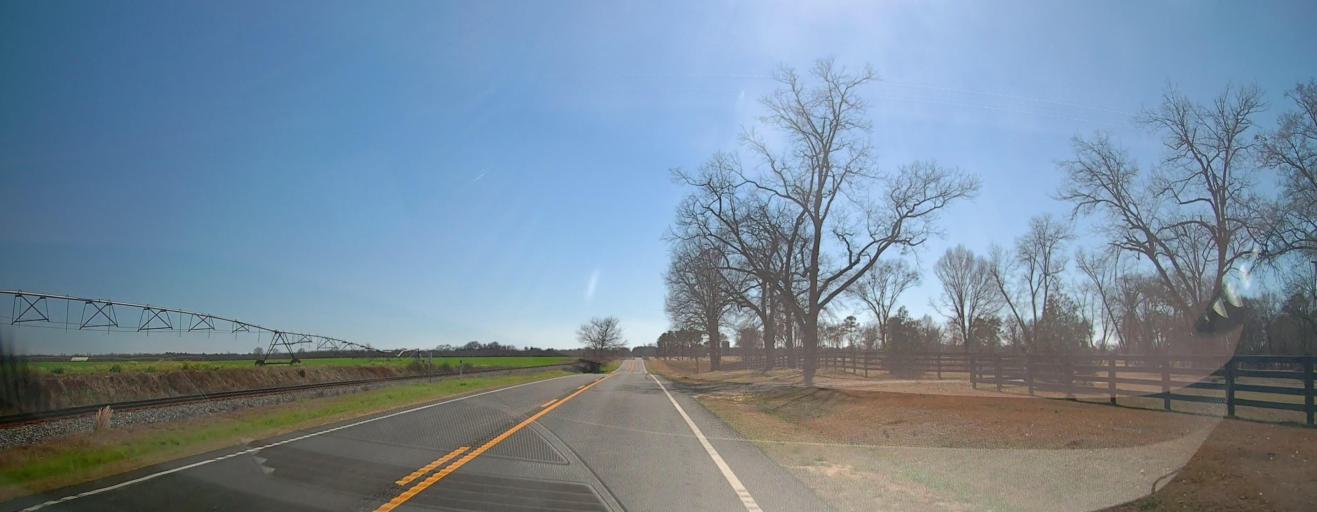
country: US
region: Georgia
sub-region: Macon County
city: Marshallville
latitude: 32.4772
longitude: -83.9335
